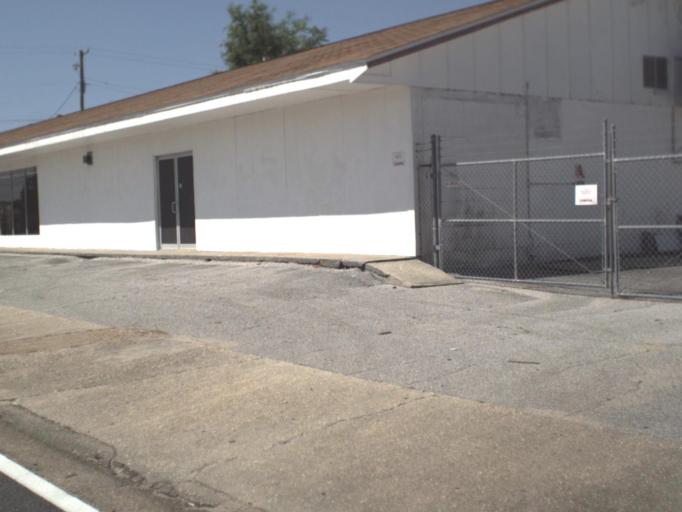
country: US
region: Florida
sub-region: Escambia County
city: Pensacola
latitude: 30.4233
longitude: -87.2412
